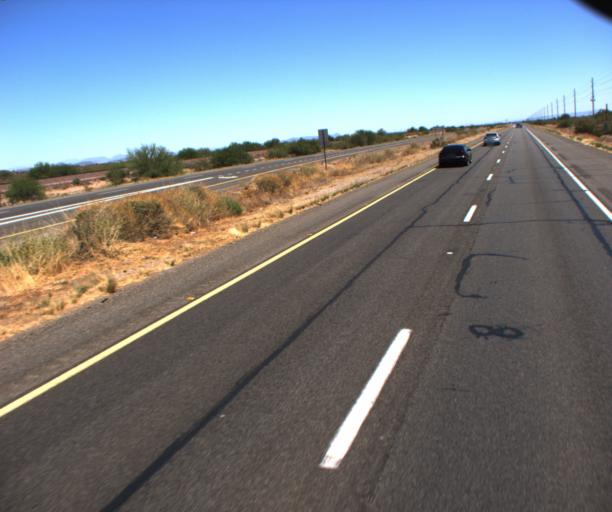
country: US
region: Arizona
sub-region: Maricopa County
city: Sun City West
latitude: 33.7257
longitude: -112.4620
